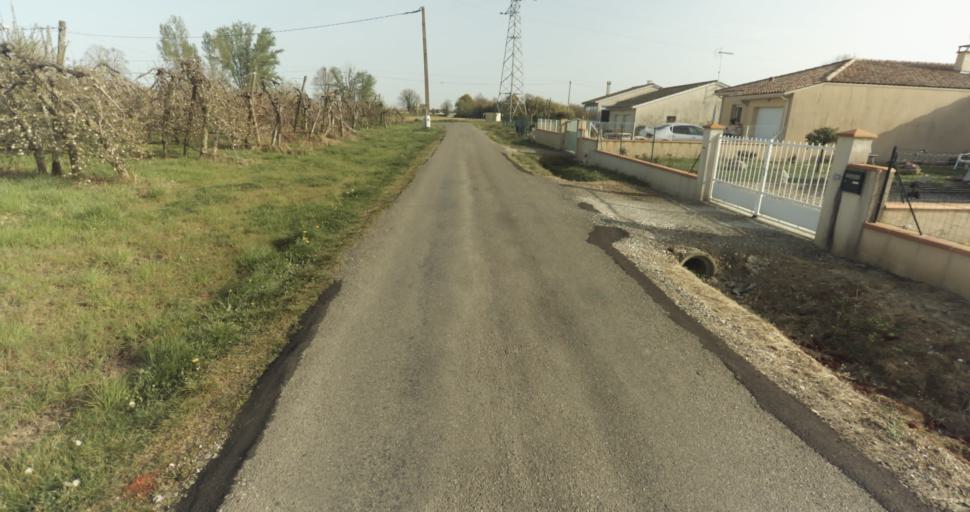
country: FR
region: Midi-Pyrenees
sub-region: Departement du Tarn-et-Garonne
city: Moissac
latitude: 44.1146
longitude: 1.1207
